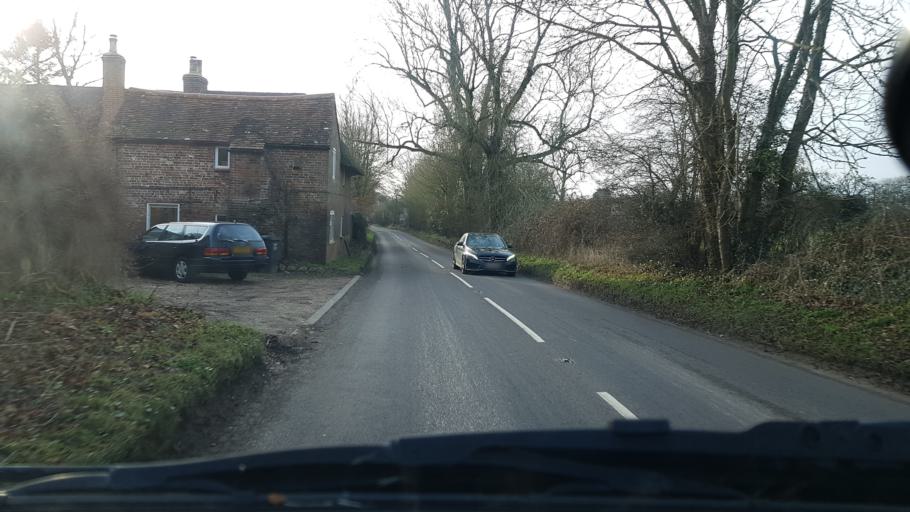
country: GB
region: England
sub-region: Wiltshire
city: Pewsey
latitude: 51.3458
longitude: -1.7513
